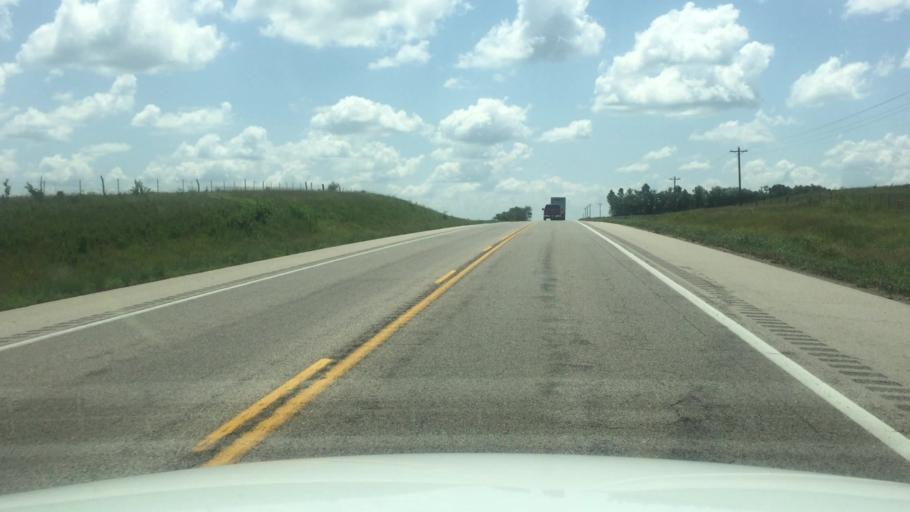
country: US
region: Kansas
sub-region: Brown County
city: Horton
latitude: 39.6786
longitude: -95.7306
